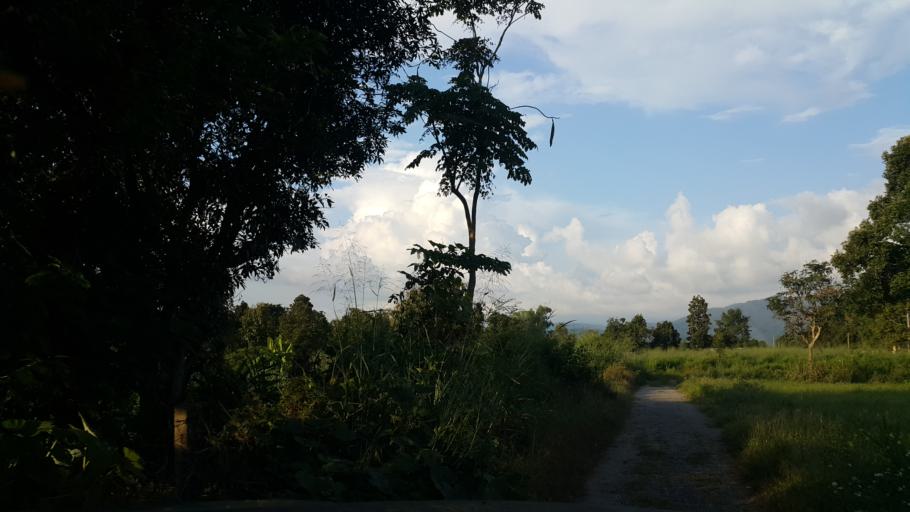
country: TH
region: Chiang Mai
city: Mae On
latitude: 18.7438
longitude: 99.2518
